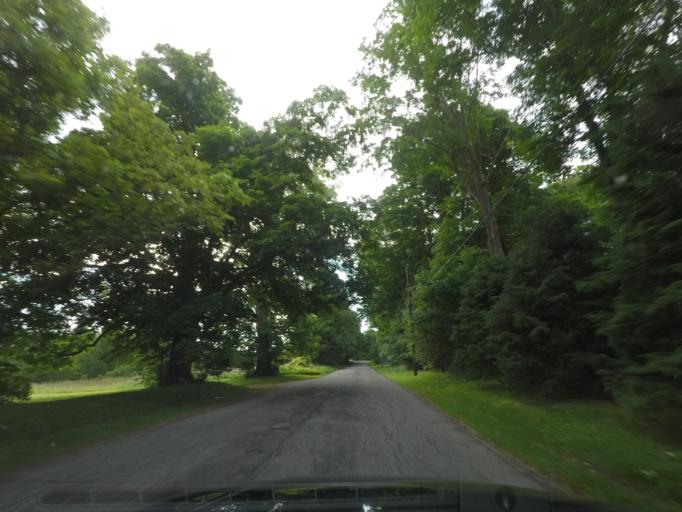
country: US
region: New York
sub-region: Dutchess County
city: Pine Plains
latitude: 41.9571
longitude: -73.4882
